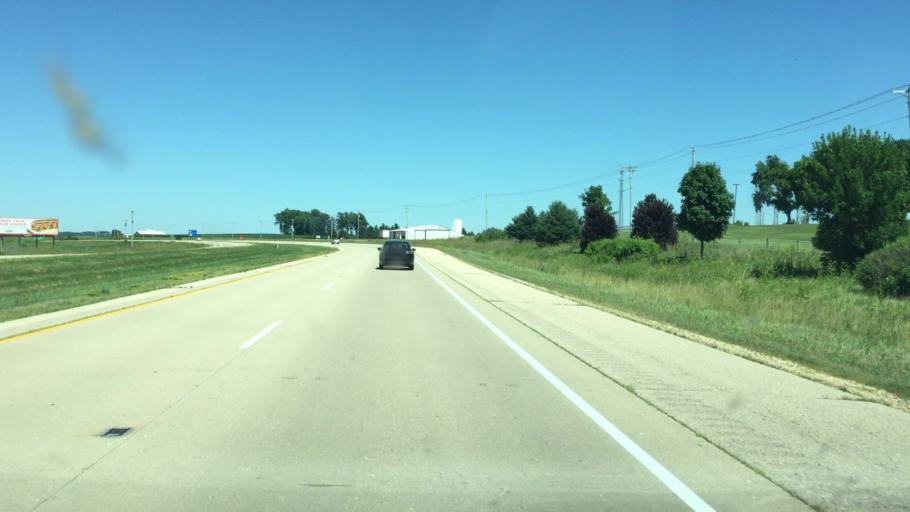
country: US
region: Wisconsin
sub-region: Iowa County
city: Mineral Point
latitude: 42.8405
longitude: -90.2091
